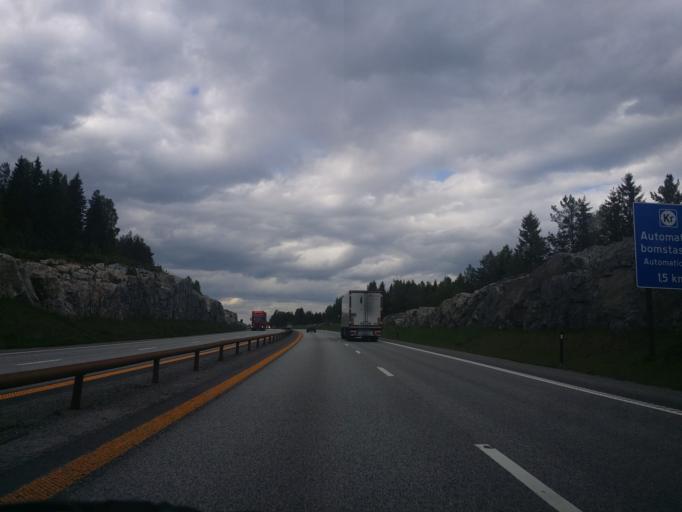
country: NO
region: Akershus
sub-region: Eidsvoll
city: Raholt
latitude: 60.2938
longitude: 11.1359
